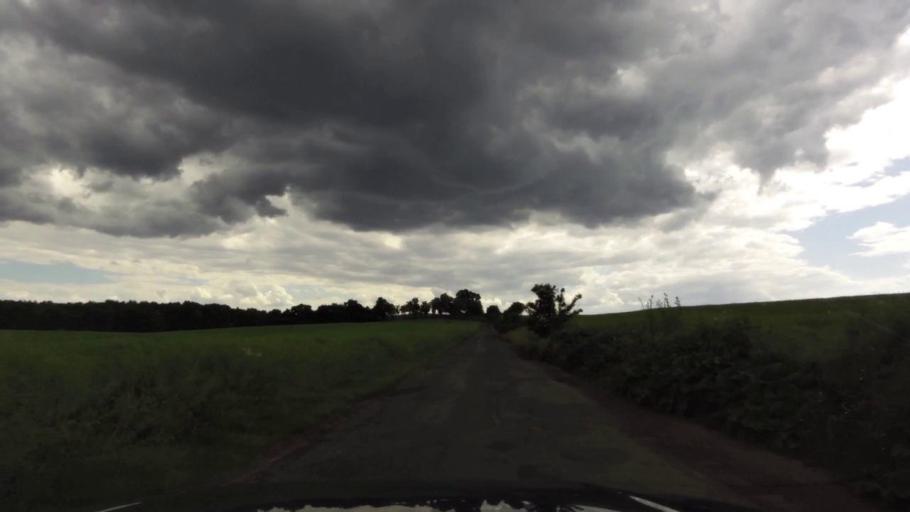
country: PL
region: West Pomeranian Voivodeship
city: Trzcinsko Zdroj
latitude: 52.9277
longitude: 14.5933
